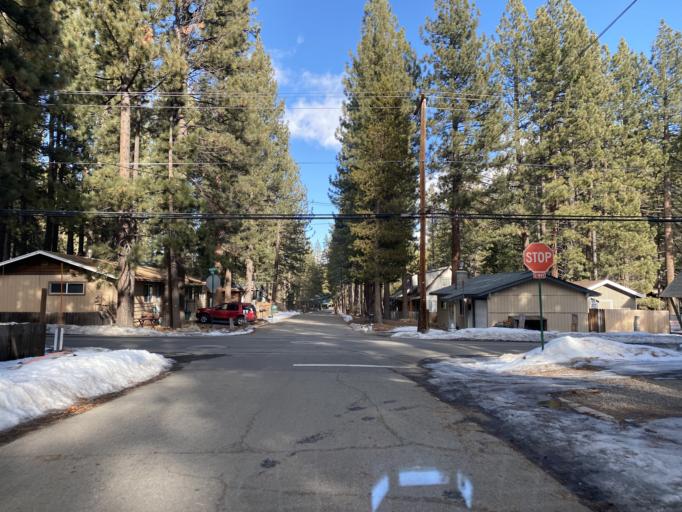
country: US
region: California
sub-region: El Dorado County
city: South Lake Tahoe
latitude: 38.9238
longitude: -119.9782
